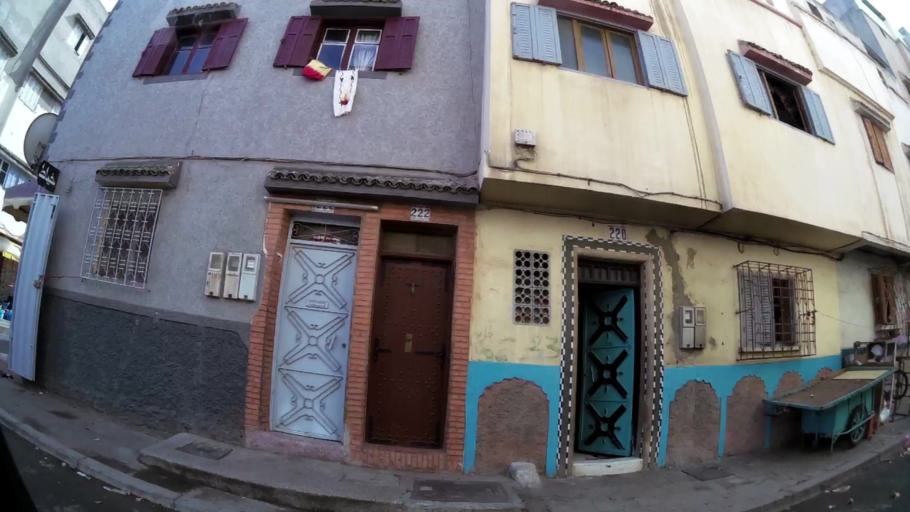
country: MA
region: Grand Casablanca
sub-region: Mohammedia
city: Mohammedia
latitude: 33.6818
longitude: -7.3774
